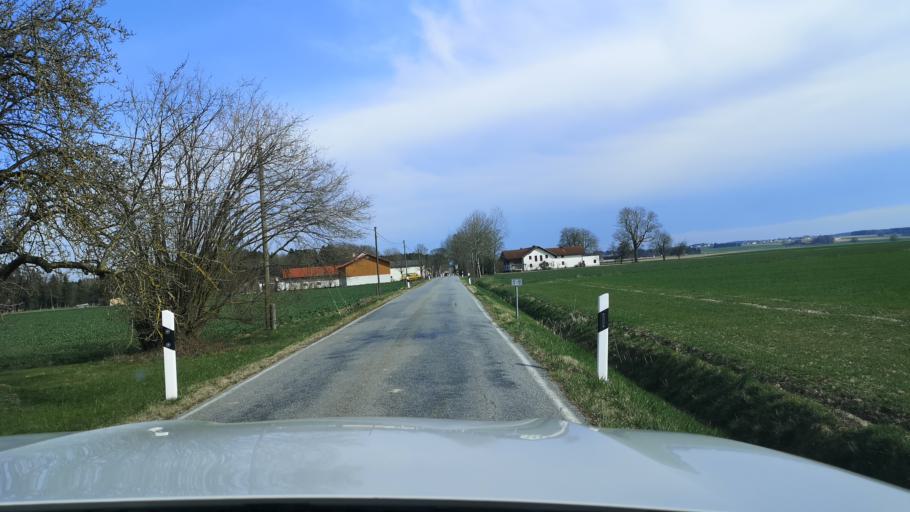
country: DE
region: Bavaria
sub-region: Upper Bavaria
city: Pastetten
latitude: 48.2167
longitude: 11.9595
